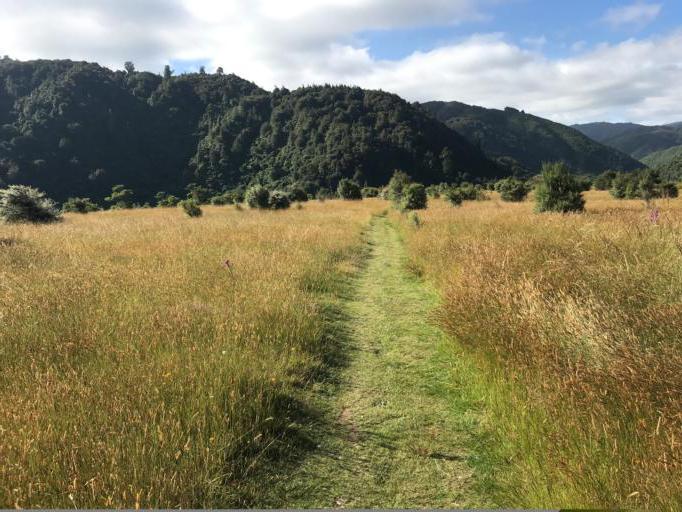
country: NZ
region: Wellington
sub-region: Kapiti Coast District
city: Otaki
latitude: -40.8742
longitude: 175.2348
